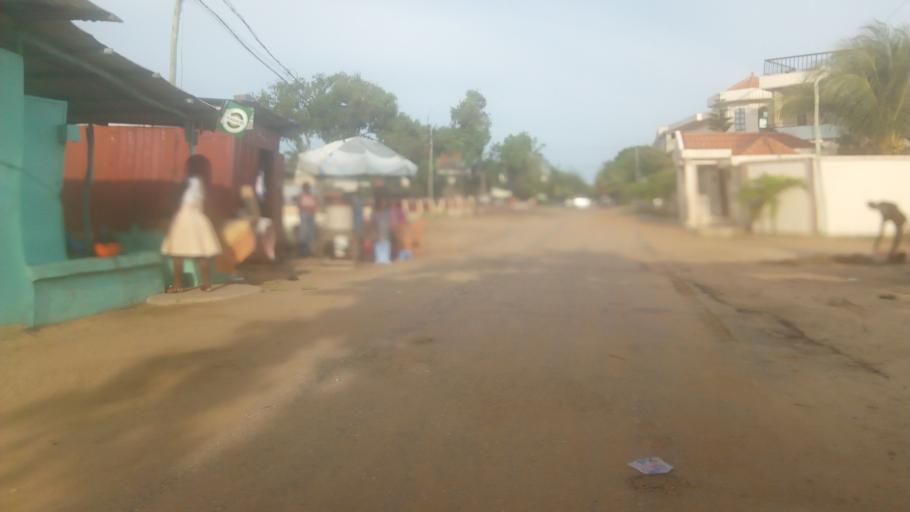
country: TG
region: Maritime
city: Lome
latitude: 6.1631
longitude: 1.3258
